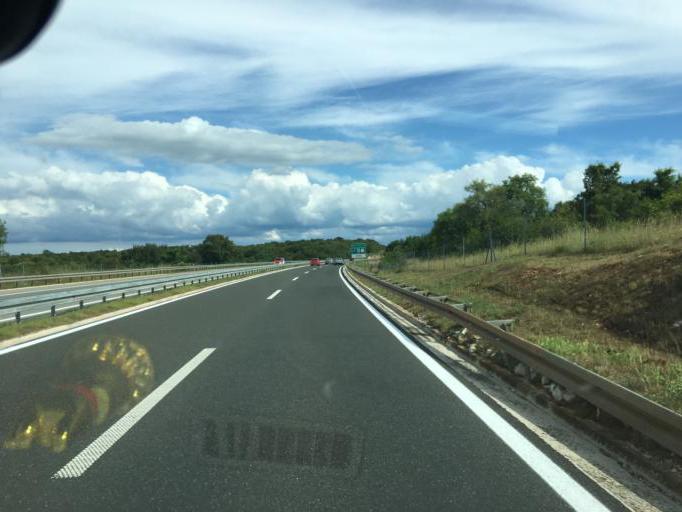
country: HR
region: Istarska
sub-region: Grad Rovinj
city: Rovinj
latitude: 45.1368
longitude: 13.7656
